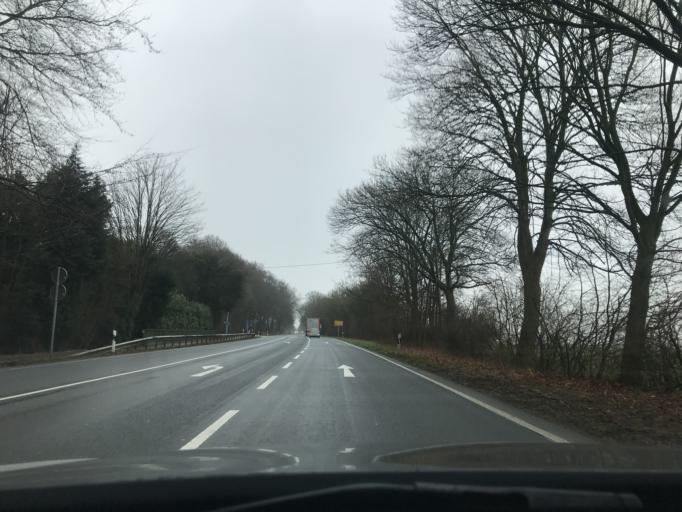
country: DE
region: North Rhine-Westphalia
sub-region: Regierungsbezirk Dusseldorf
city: Kleve
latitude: 51.7373
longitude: 6.1599
